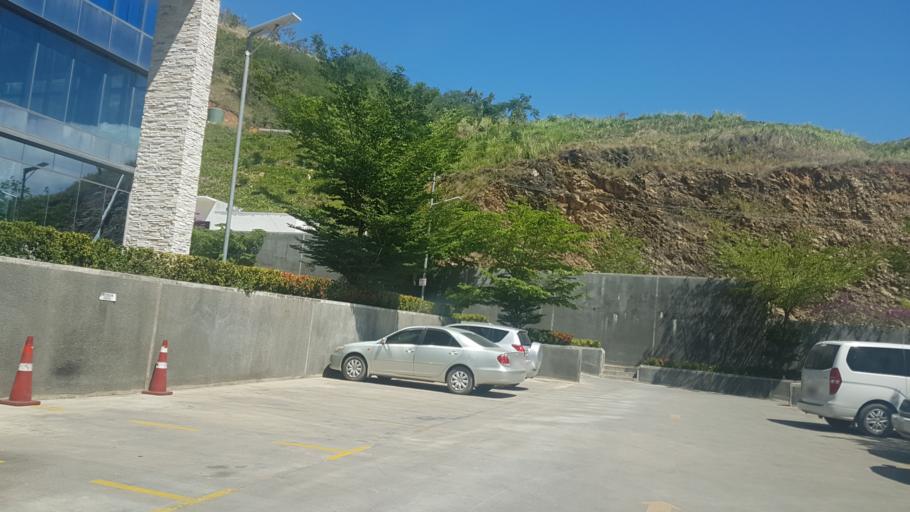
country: PG
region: National Capital
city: Port Moresby
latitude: -9.4403
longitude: 147.1773
